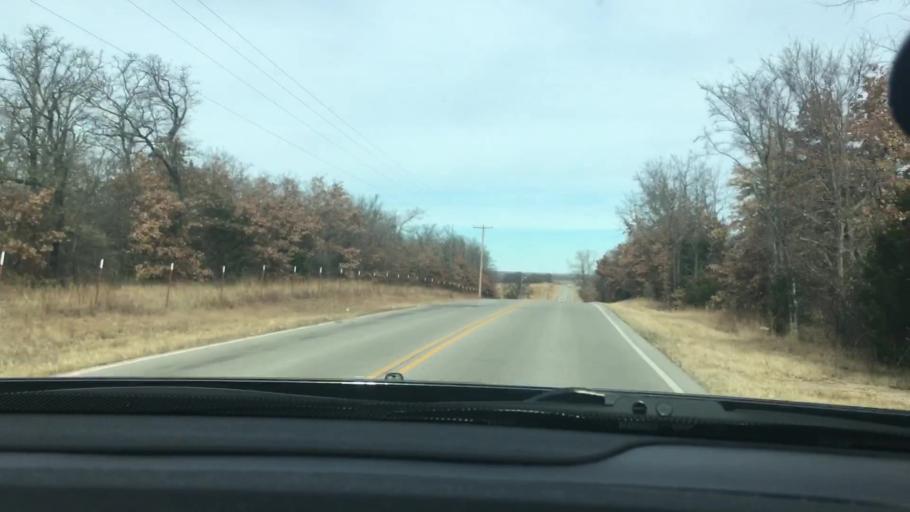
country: US
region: Oklahoma
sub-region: Carter County
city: Ardmore
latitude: 34.1781
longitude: -97.0731
